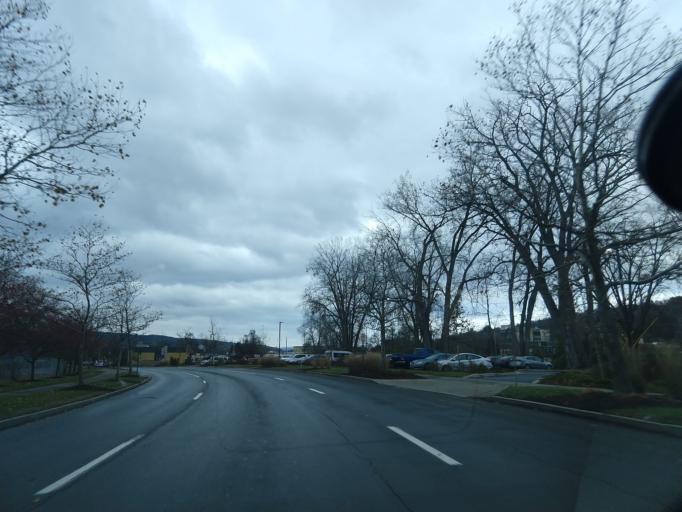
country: US
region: New York
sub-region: Tompkins County
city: Ithaca
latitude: 42.4438
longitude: -76.5105
